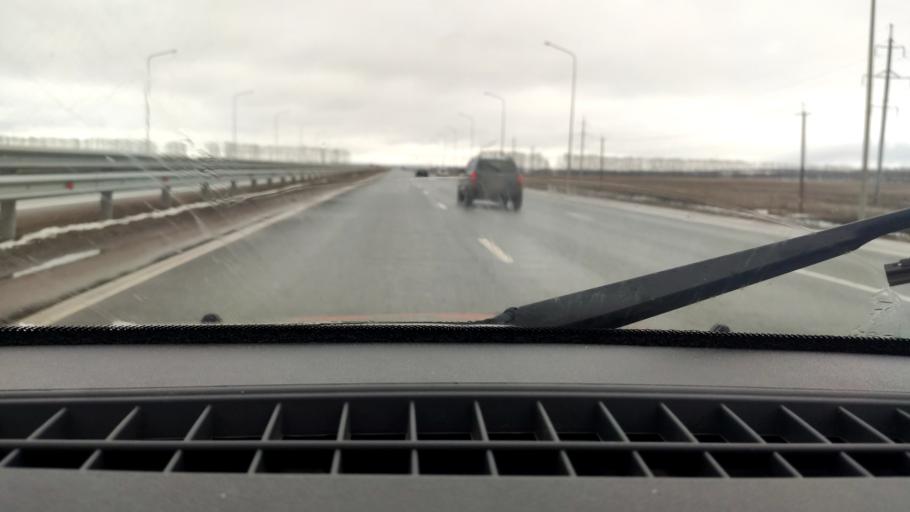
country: RU
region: Bashkortostan
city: Asanovo
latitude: 54.8910
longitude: 55.6509
